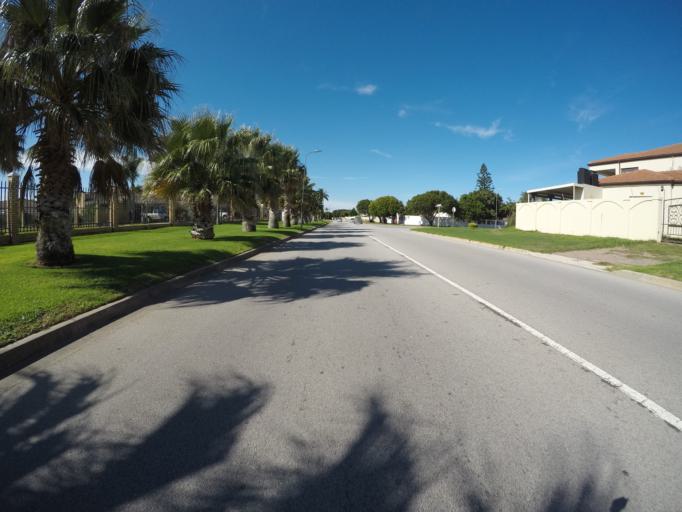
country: ZA
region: Eastern Cape
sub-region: Nelson Mandela Bay Metropolitan Municipality
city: Port Elizabeth
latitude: -33.9906
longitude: 25.6524
